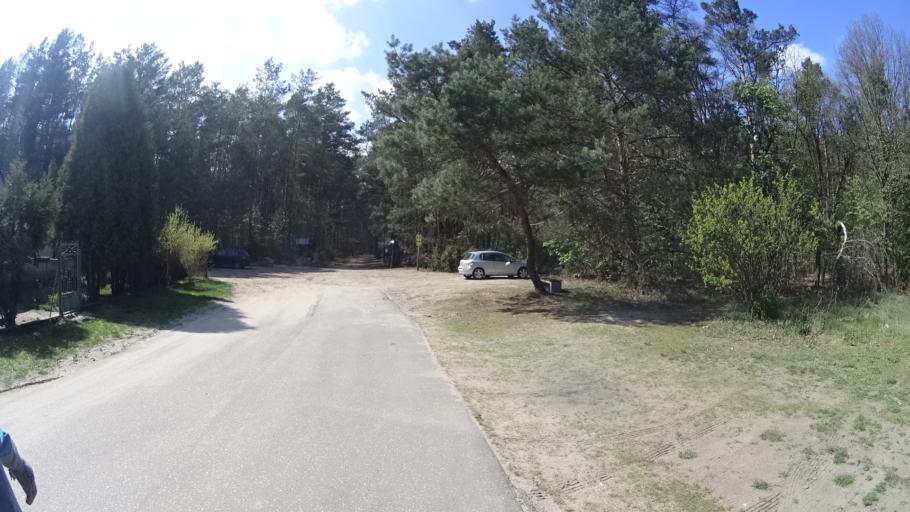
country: PL
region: Masovian Voivodeship
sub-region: Powiat warszawski zachodni
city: Truskaw
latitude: 52.3180
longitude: 20.7976
